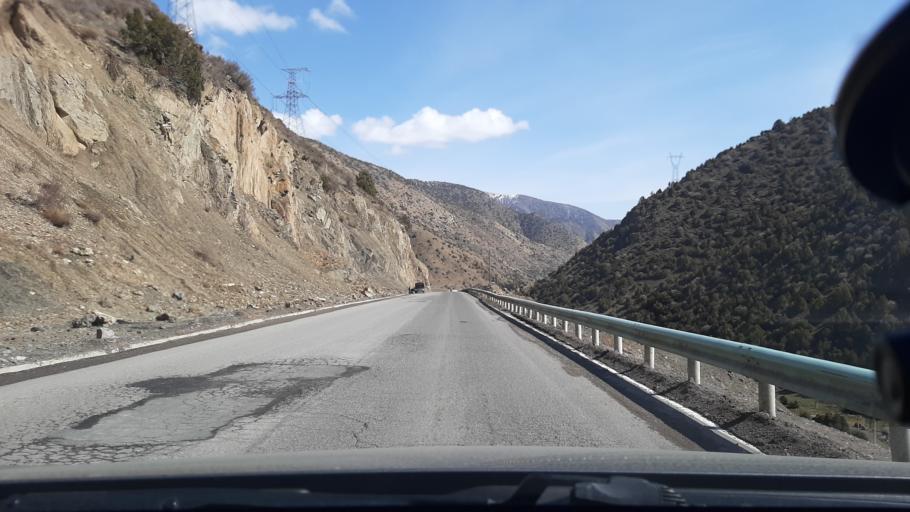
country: TJ
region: Viloyati Sughd
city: Ayni
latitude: 39.5687
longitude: 68.5912
